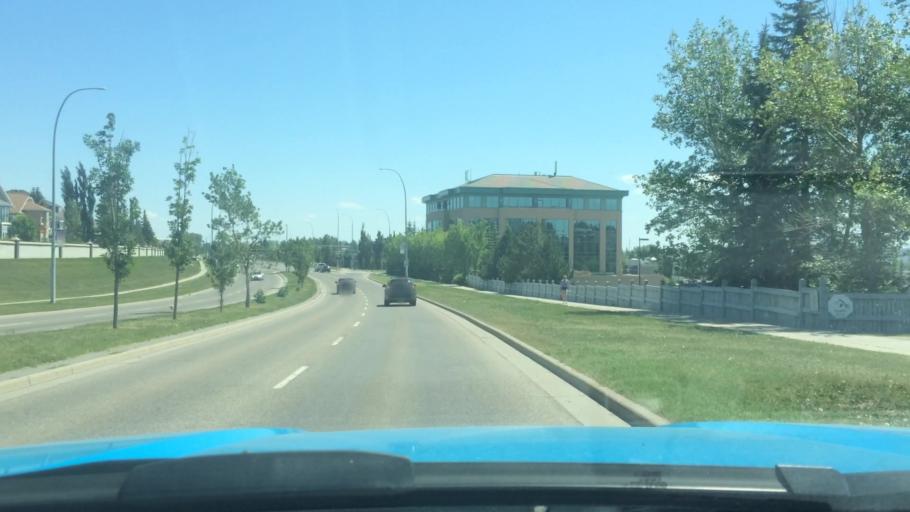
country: CA
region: Alberta
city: Calgary
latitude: 51.1312
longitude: -114.2022
